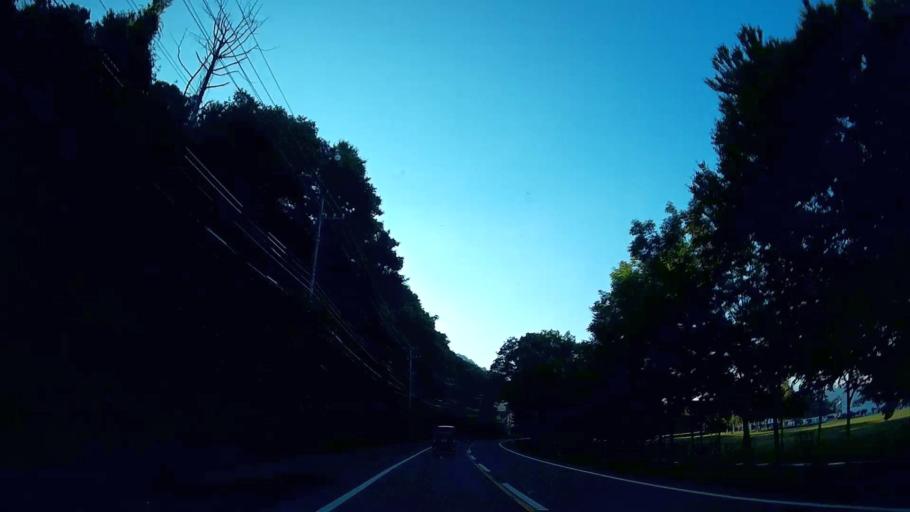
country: JP
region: Hokkaido
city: Date
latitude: 42.5664
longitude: 140.8073
